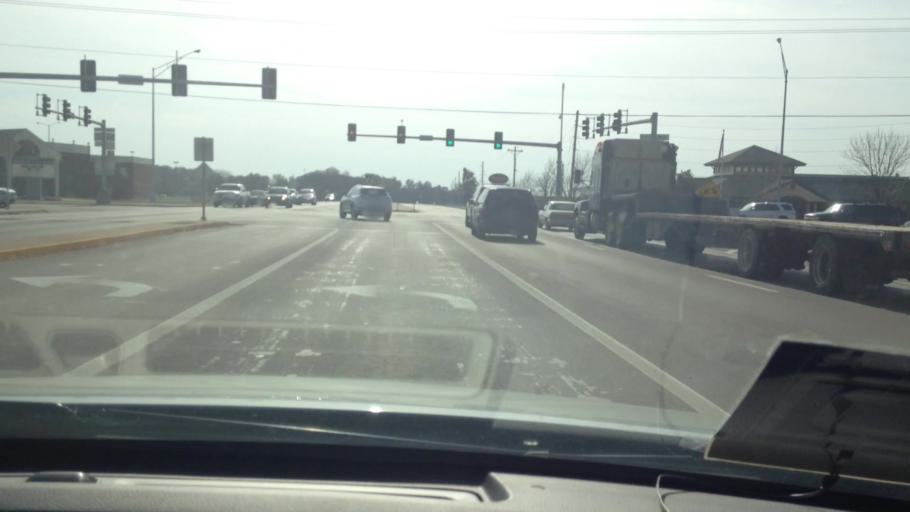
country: US
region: Missouri
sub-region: Henry County
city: Clinton
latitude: 38.3668
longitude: -93.7521
